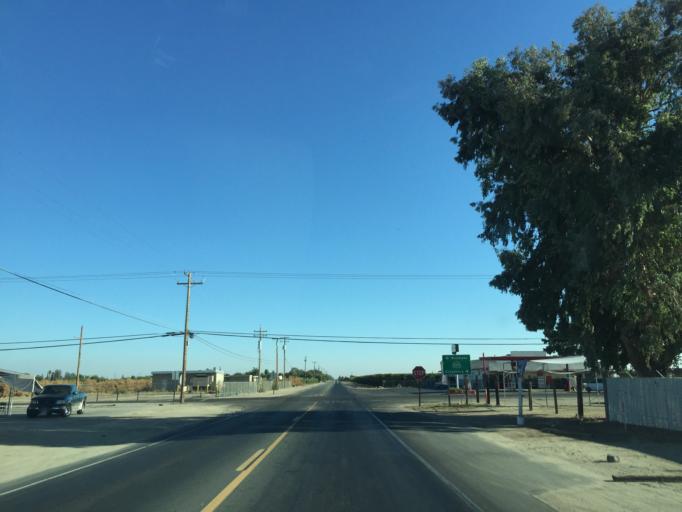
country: US
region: California
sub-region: Tulare County
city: London
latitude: 36.5180
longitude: -119.4487
